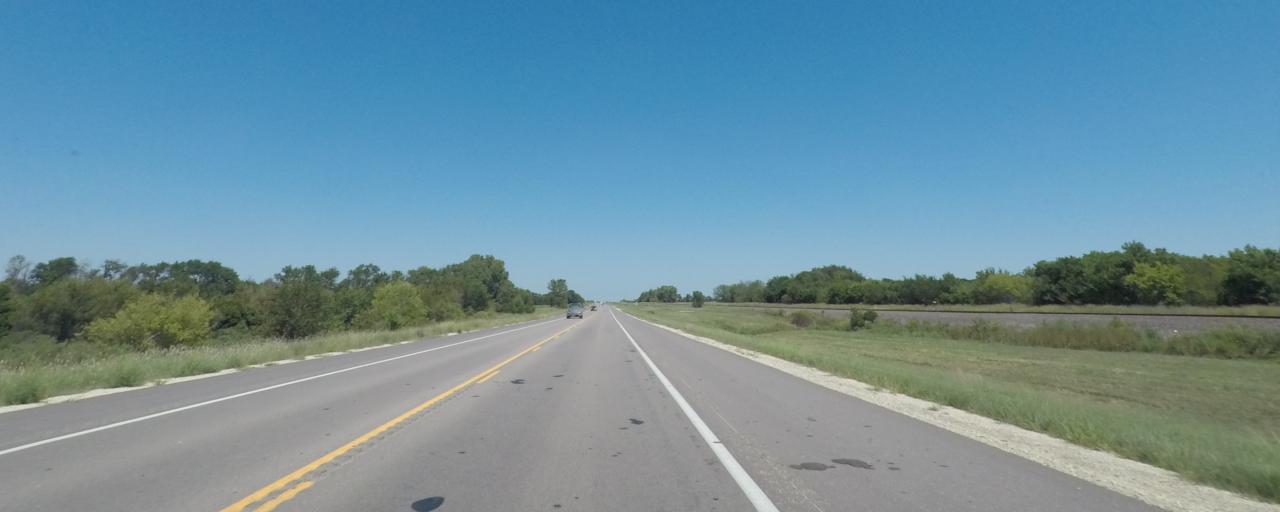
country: US
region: Kansas
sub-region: Harvey County
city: North Newton
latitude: 38.0770
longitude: -97.2972
